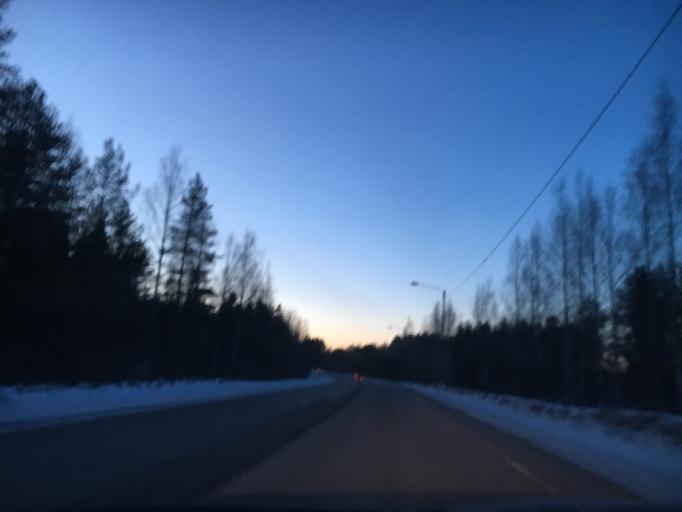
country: FI
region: Kainuu
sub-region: Kajaani
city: Kajaani
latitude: 64.2007
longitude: 27.7465
